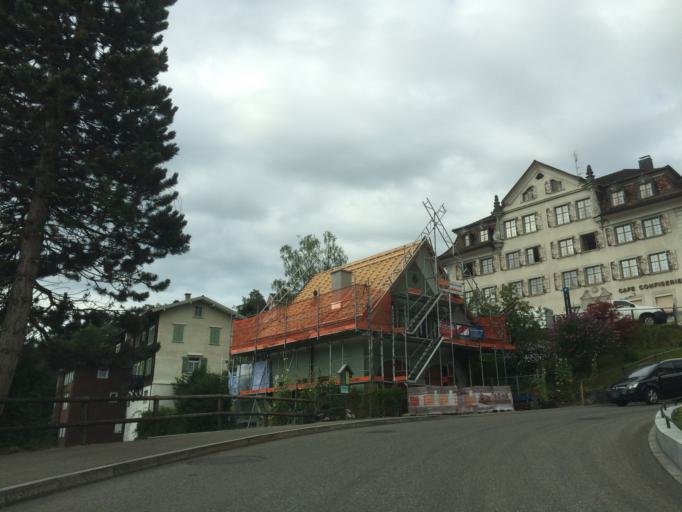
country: CH
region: Appenzell Ausserrhoden
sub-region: Bezirk Mittelland
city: Trogen
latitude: 47.4075
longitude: 9.4654
